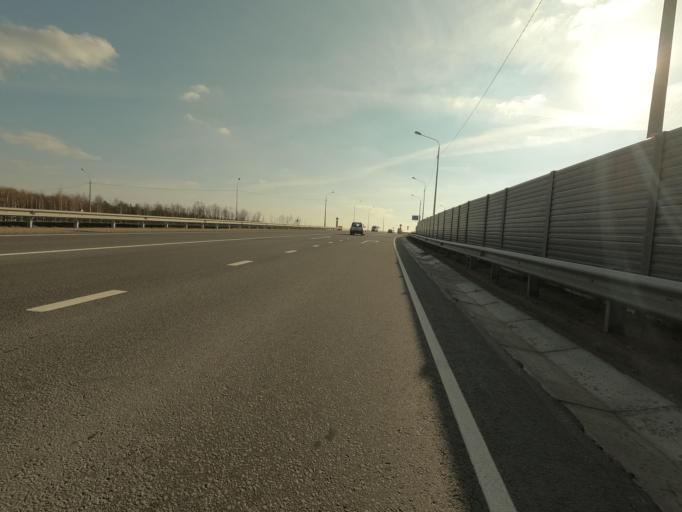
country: RU
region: Leningrad
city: Mga
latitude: 59.7587
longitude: 31.0936
